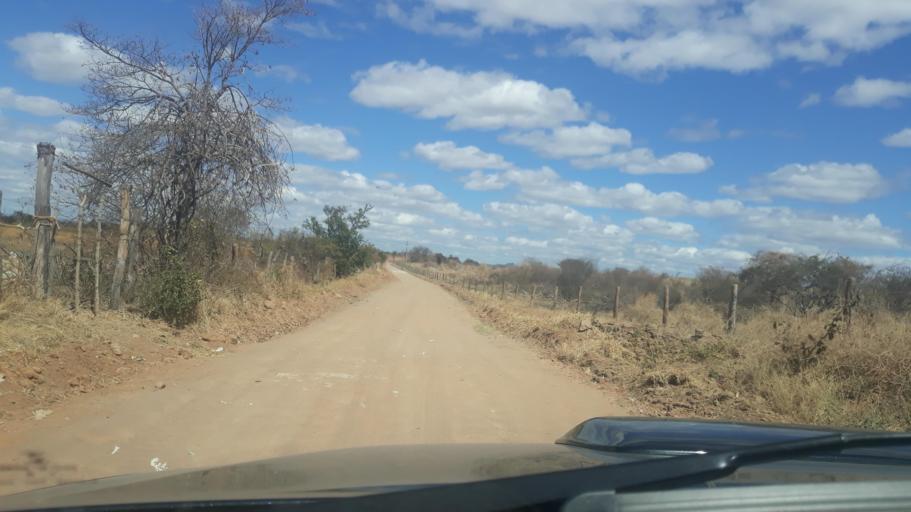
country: BR
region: Bahia
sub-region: Riacho De Santana
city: Riacho de Santana
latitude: -13.8944
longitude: -42.8485
